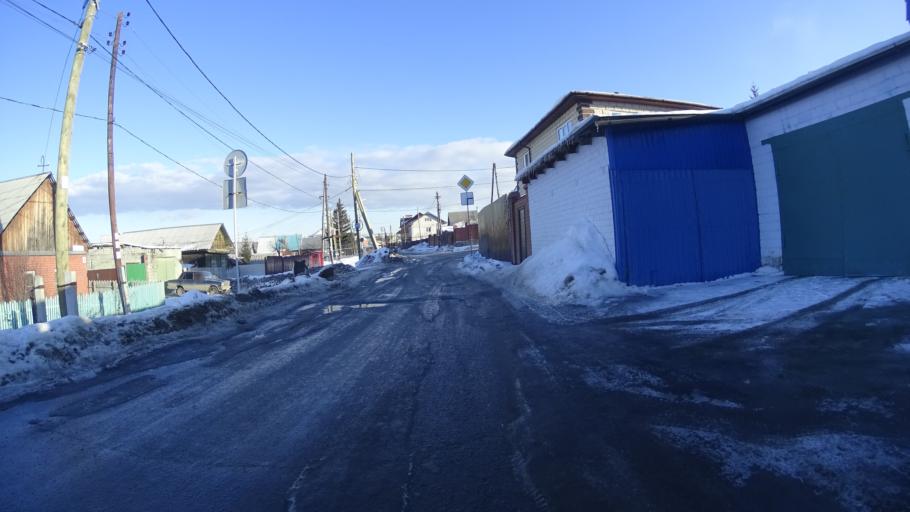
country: RU
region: Chelyabinsk
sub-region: Gorod Chelyabinsk
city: Chelyabinsk
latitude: 55.1543
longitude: 61.3099
